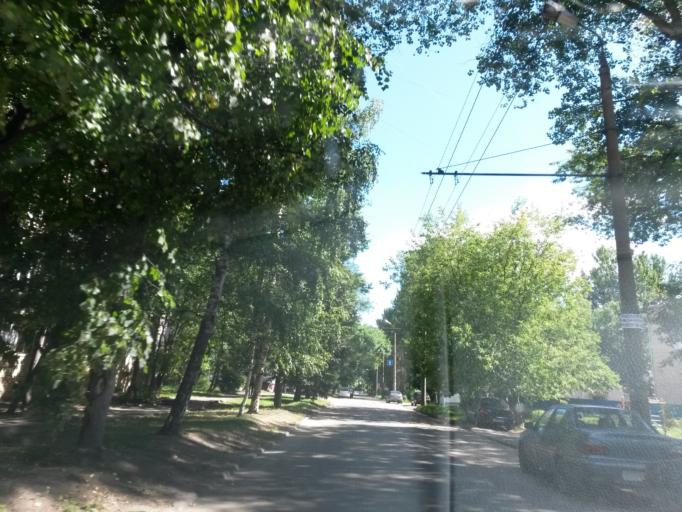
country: RU
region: Jaroslavl
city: Yaroslavl
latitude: 57.5809
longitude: 39.8377
